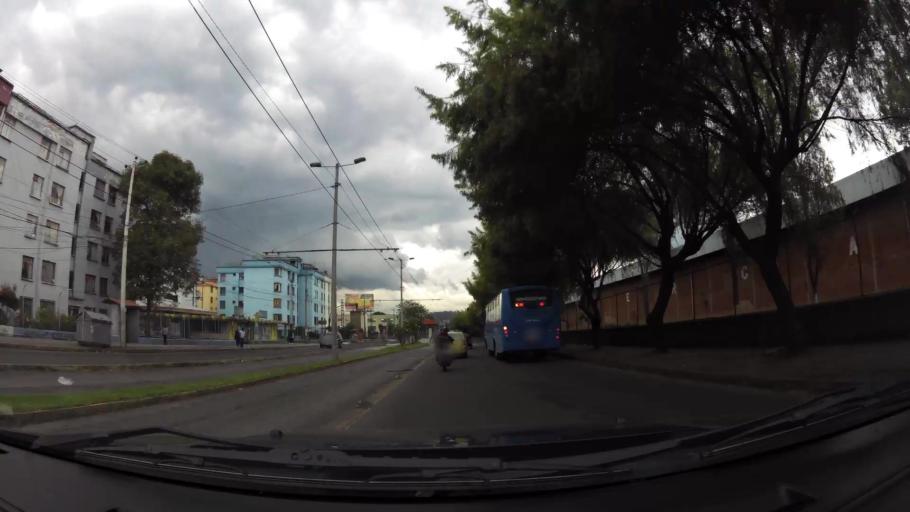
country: EC
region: Pichincha
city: Quito
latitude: -0.2708
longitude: -78.5361
